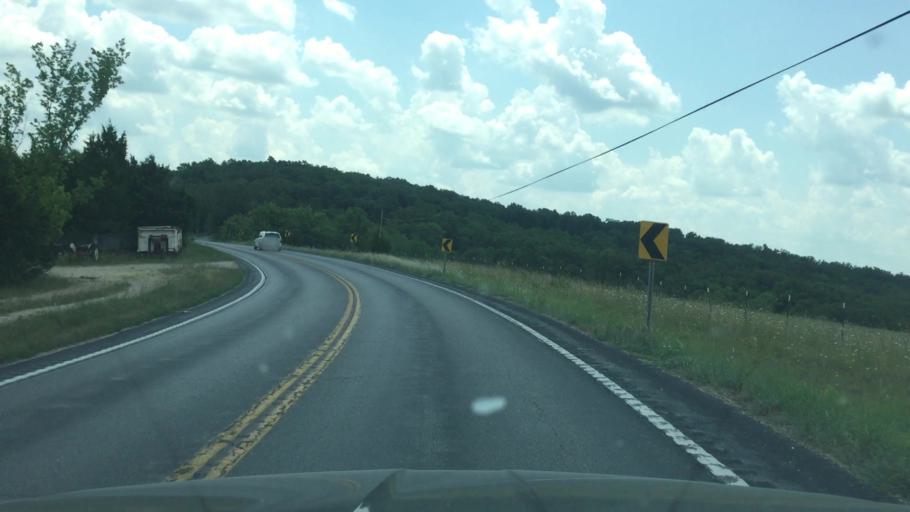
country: US
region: Missouri
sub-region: Miller County
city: Tuscumbia
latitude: 38.1009
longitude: -92.4984
